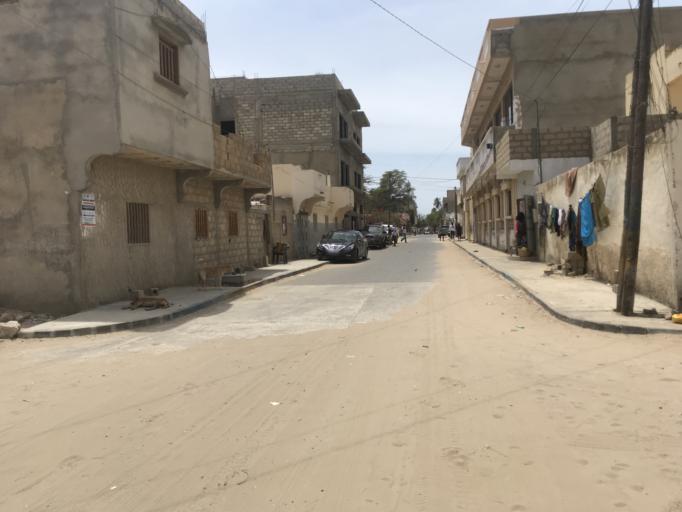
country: SN
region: Saint-Louis
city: Saint-Louis
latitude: 16.0224
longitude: -16.4879
